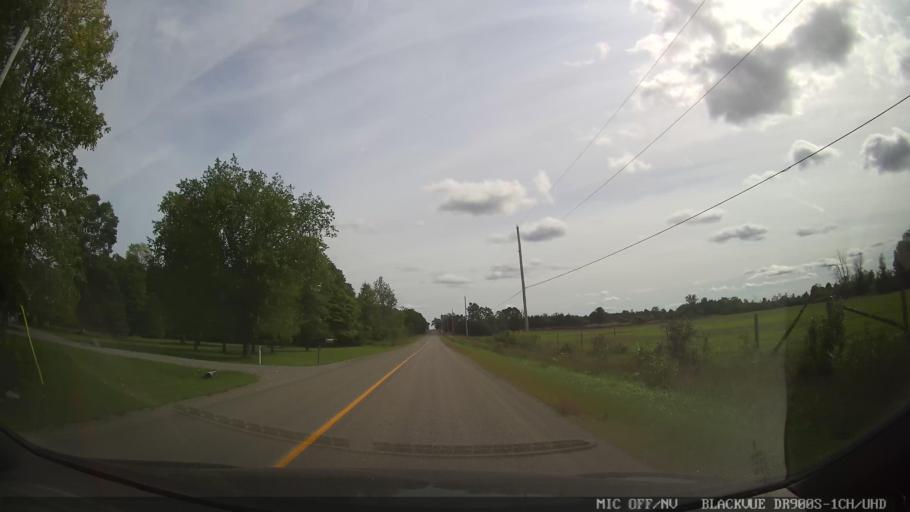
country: CA
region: Ontario
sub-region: Lanark County
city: Smiths Falls
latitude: 44.8882
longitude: -75.9198
